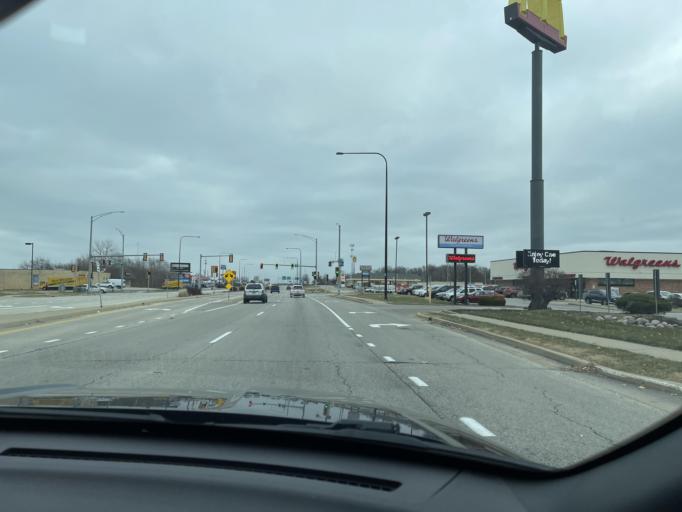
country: US
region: Illinois
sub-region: Sangamon County
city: Grandview
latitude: 39.8019
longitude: -89.6048
